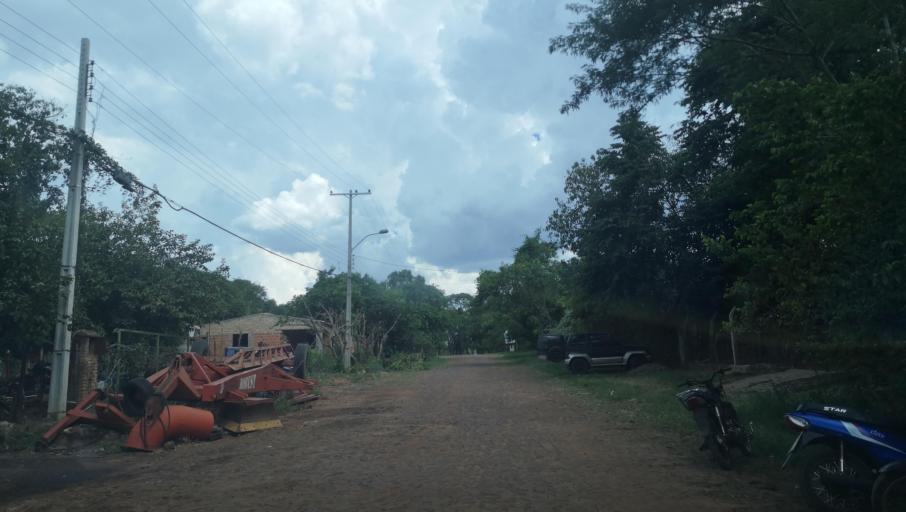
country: PY
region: Misiones
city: Santa Maria
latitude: -26.8875
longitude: -57.0104
